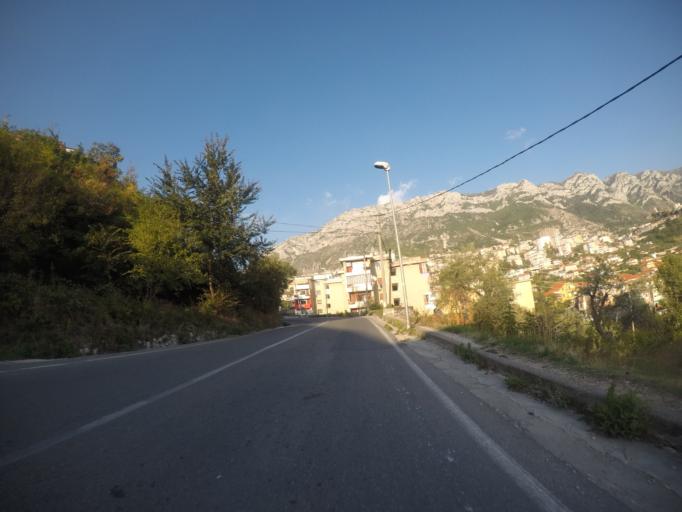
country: AL
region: Durres
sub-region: Rrethi i Krujes
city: Kruje
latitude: 41.5100
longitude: 19.7838
